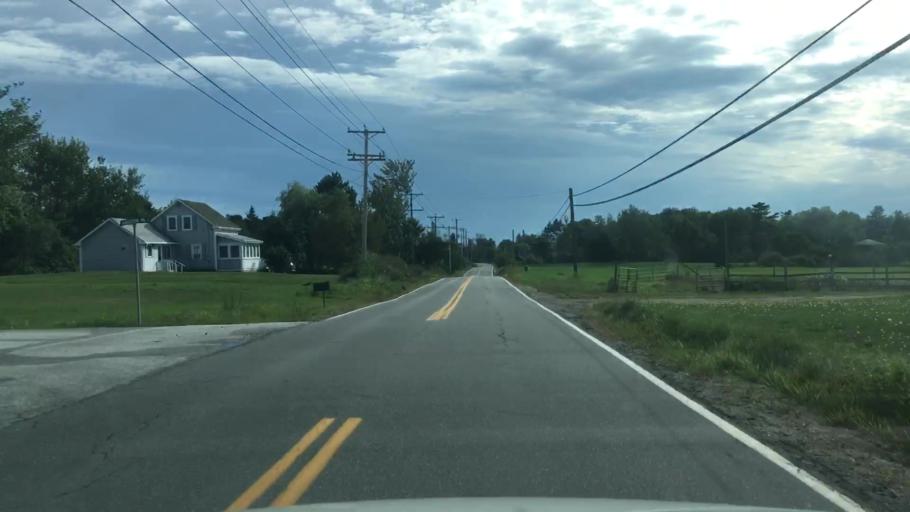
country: US
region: Maine
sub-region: Hancock County
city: Ellsworth
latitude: 44.5045
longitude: -68.4183
